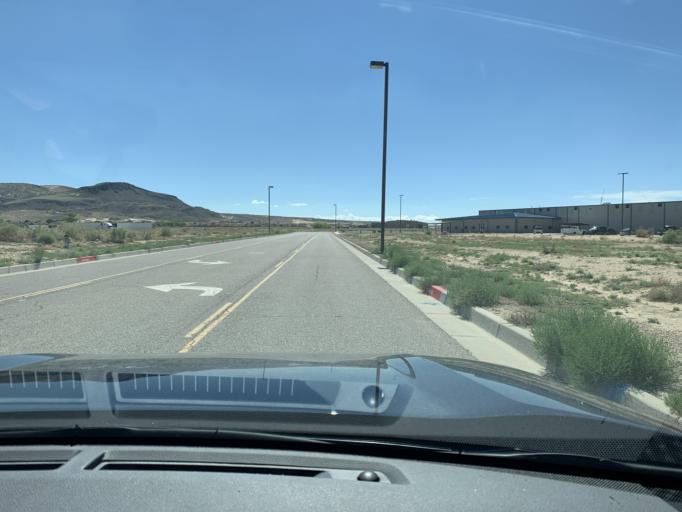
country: US
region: New Mexico
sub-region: Valencia County
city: Los Lunas
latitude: 34.8217
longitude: -106.7660
